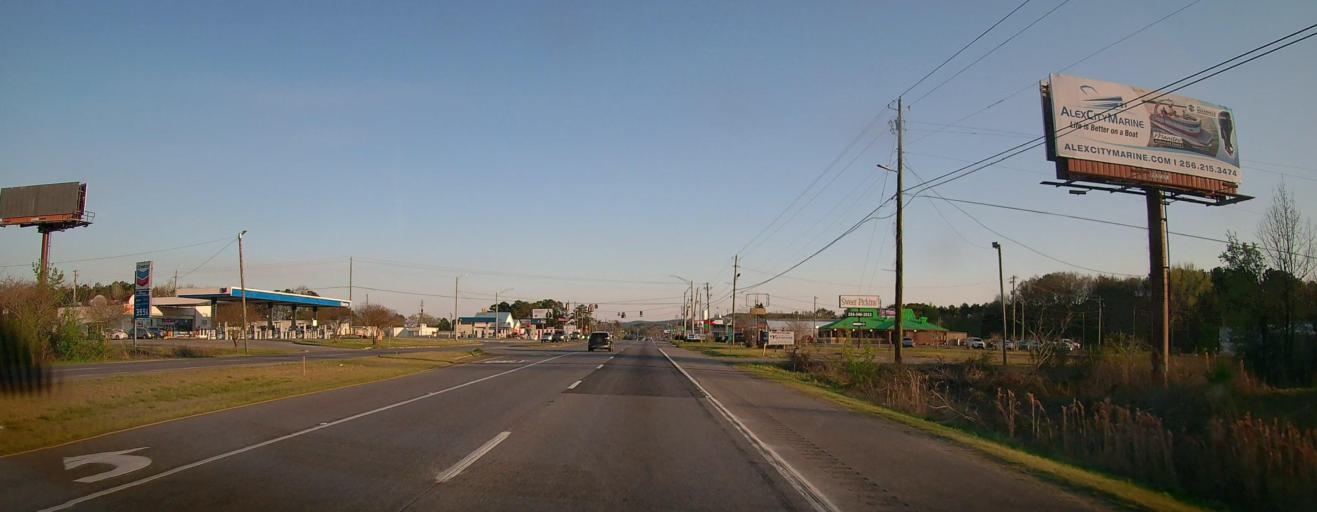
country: US
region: Alabama
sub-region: Talladega County
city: Childersburg
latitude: 33.2865
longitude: -86.3634
